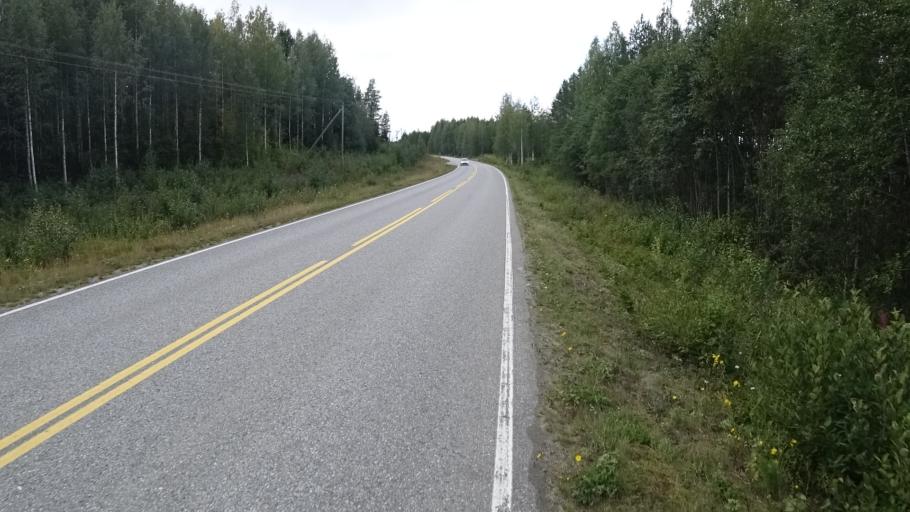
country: FI
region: North Karelia
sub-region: Joensuu
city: Ilomantsi
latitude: 62.6276
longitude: 31.2632
